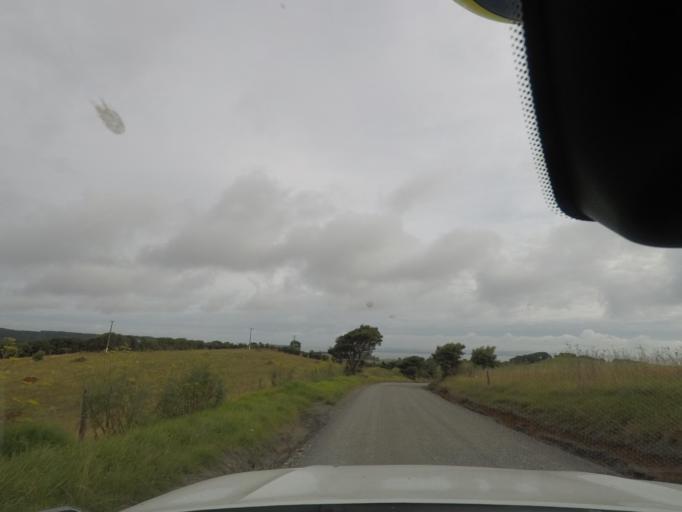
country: NZ
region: Auckland
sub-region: Auckland
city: Parakai
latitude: -36.4817
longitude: 174.2540
